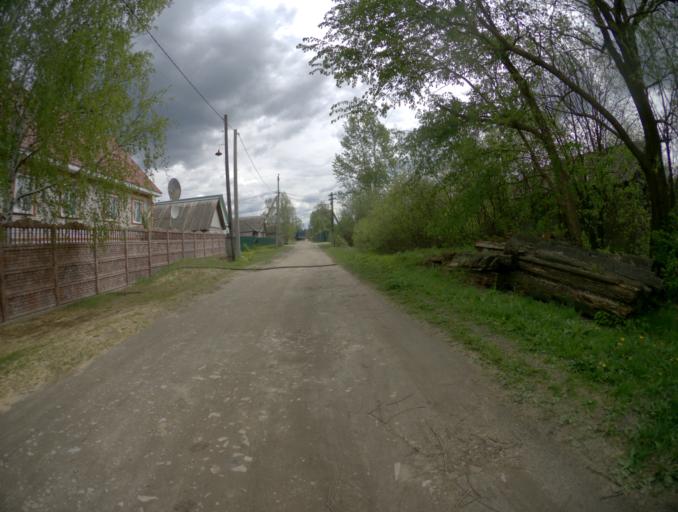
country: RU
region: Vladimir
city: Kurlovo
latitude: 55.4481
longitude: 40.6214
